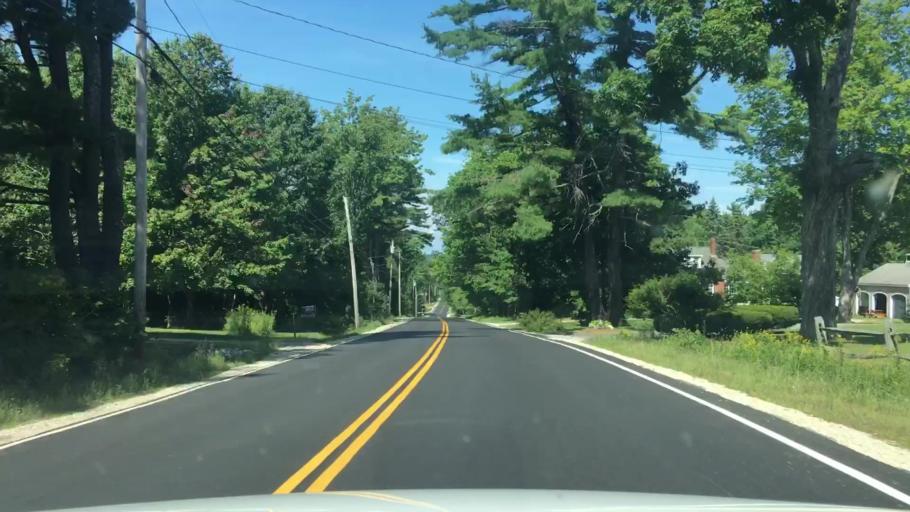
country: US
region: Maine
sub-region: Cumberland County
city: Cumberland Center
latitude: 43.7724
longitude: -70.3011
